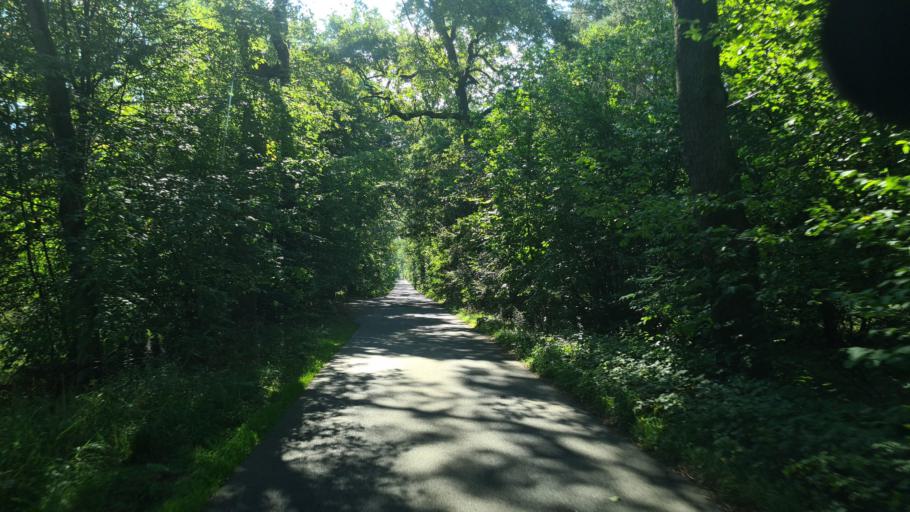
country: DE
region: Brandenburg
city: Nauen
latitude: 52.6314
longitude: 12.9341
